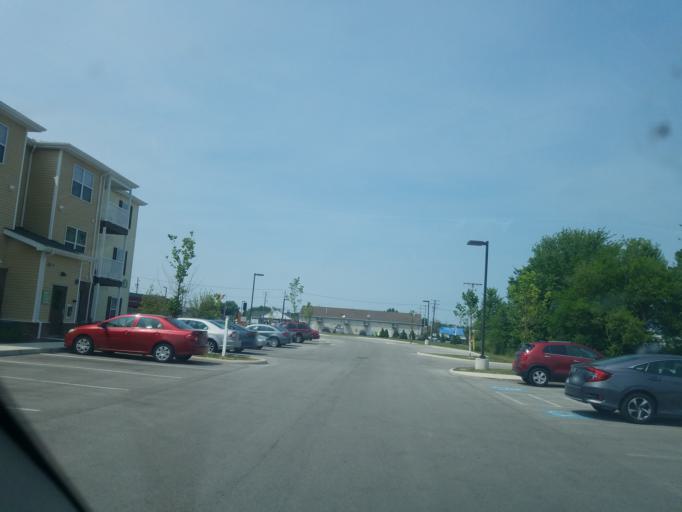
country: US
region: Ohio
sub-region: Seneca County
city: Tiffin
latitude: 41.1102
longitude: -83.2028
